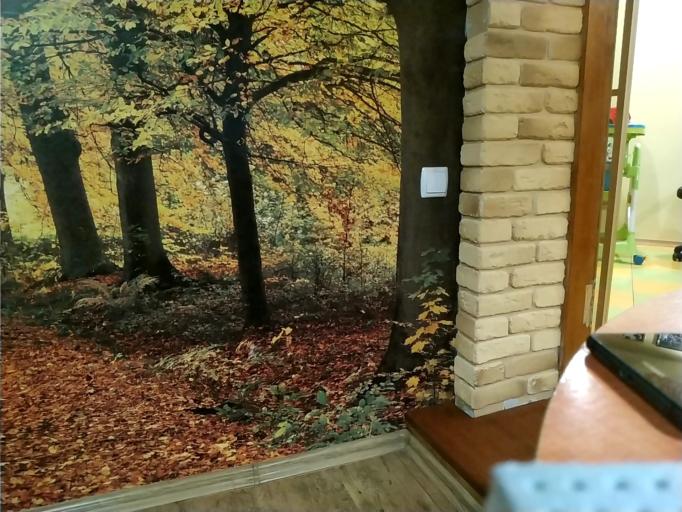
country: RU
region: Tverskaya
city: Zubtsov
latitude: 56.2563
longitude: 34.6988
